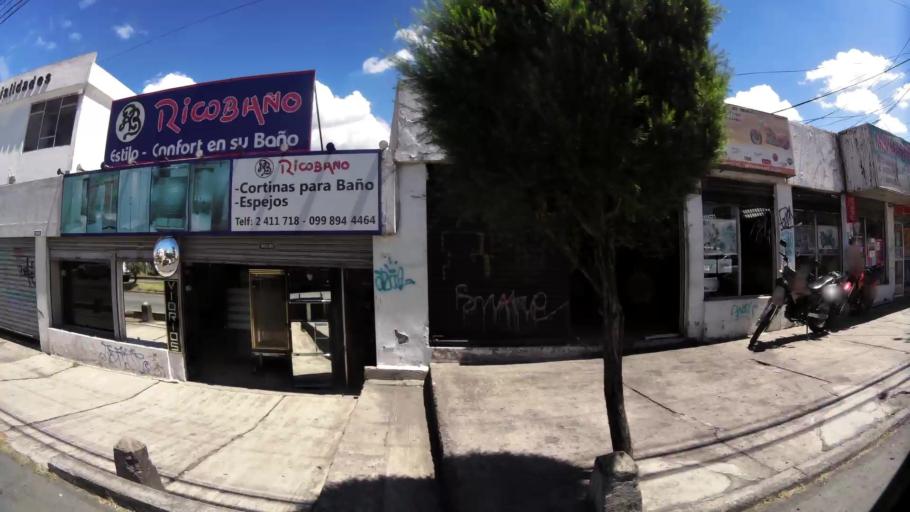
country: EC
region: Pichincha
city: Quito
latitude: -0.1359
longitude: -78.4823
